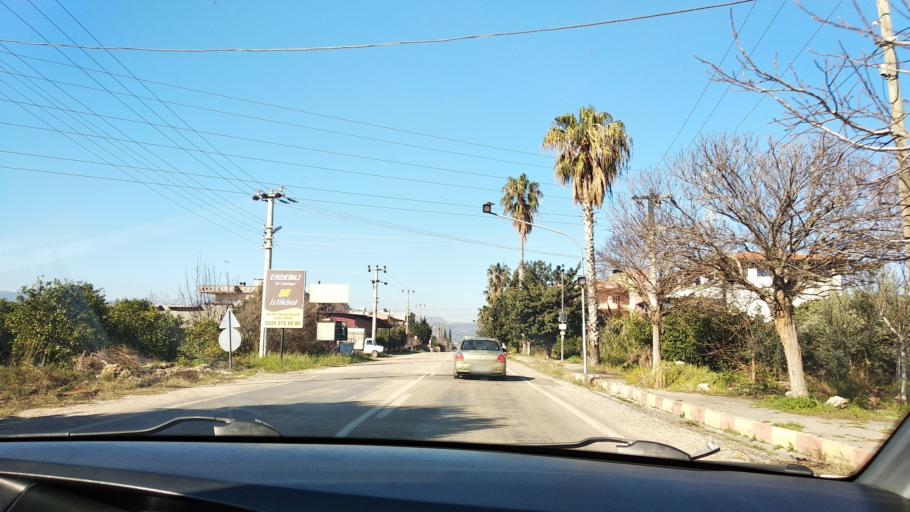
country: TR
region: Mersin
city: Tomuk
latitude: 36.6587
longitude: 34.3652
